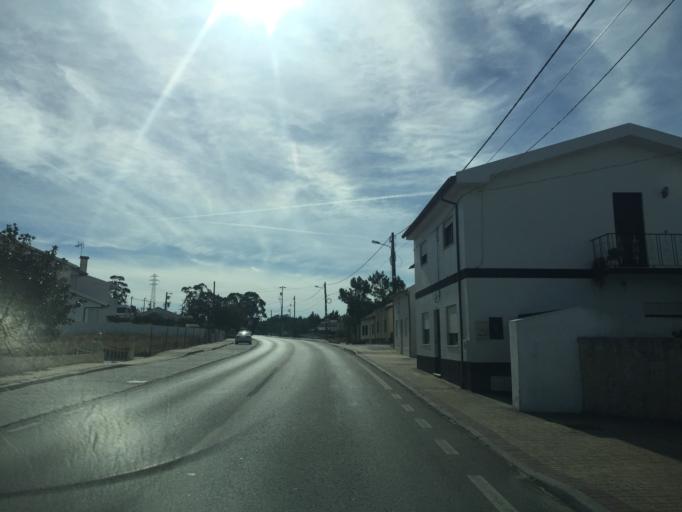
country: PT
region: Coimbra
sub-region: Figueira da Foz
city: Lavos
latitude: 40.0867
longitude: -8.8260
